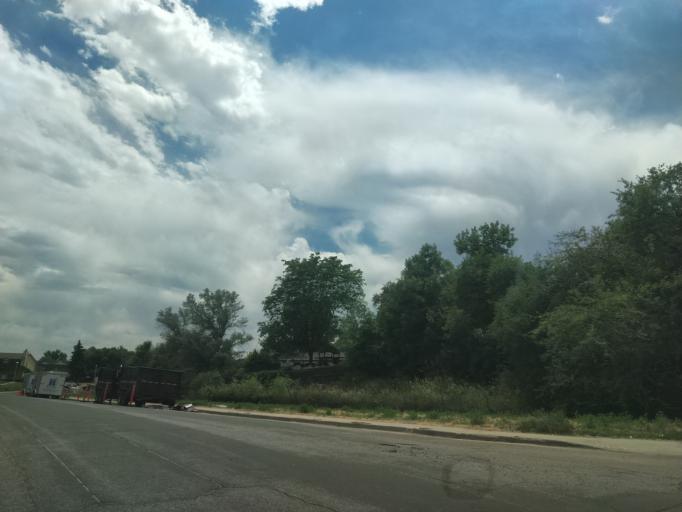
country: US
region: Colorado
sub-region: Jefferson County
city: Lakewood
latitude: 39.6917
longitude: -105.1221
